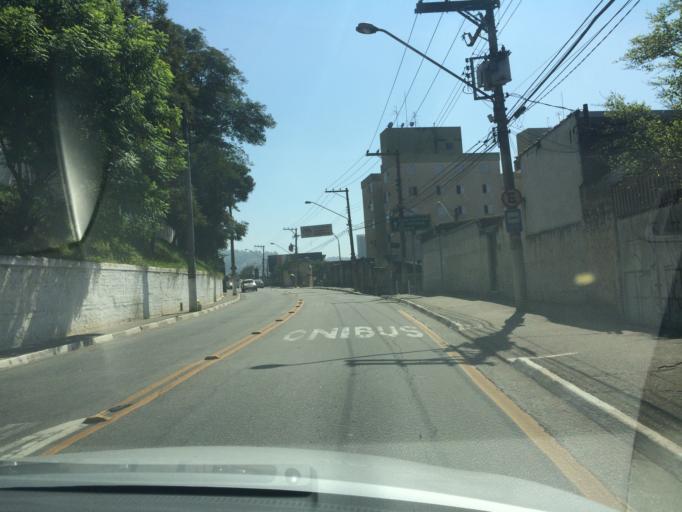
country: BR
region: Sao Paulo
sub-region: Guarulhos
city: Guarulhos
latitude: -23.4369
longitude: -46.5376
